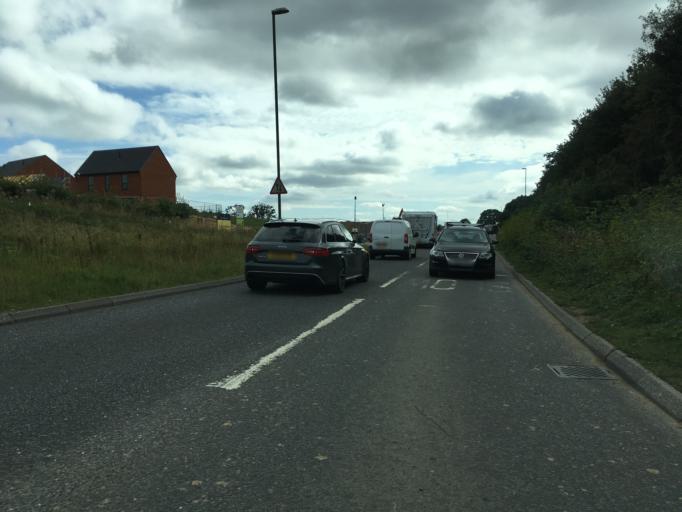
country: GB
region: England
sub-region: West Sussex
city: Broadfield
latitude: 51.0851
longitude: -0.1966
